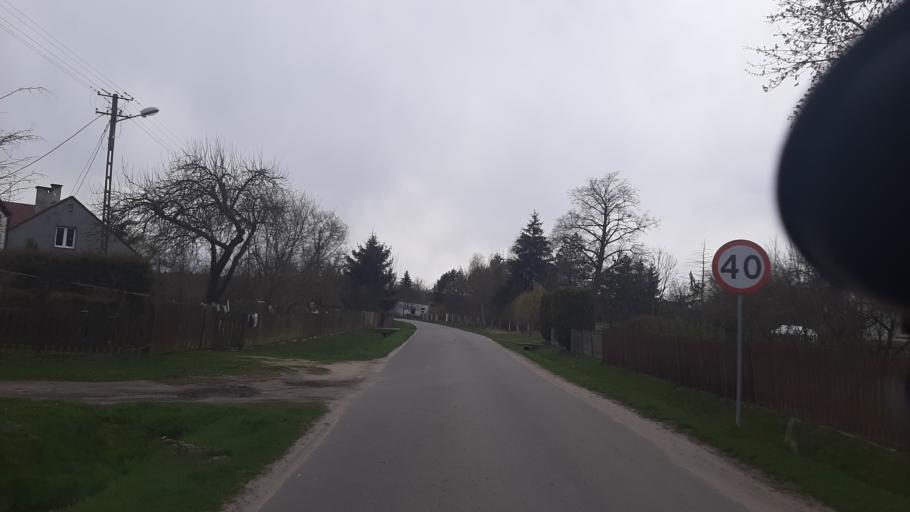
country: PL
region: Lublin Voivodeship
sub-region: Powiat lubelski
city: Niemce
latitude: 51.3852
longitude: 22.5610
